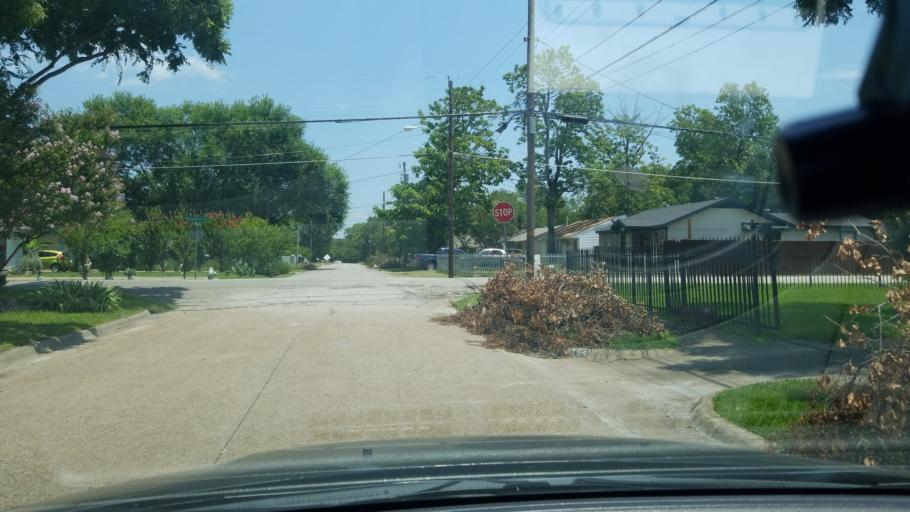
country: US
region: Texas
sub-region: Dallas County
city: Balch Springs
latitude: 32.7273
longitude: -96.6686
